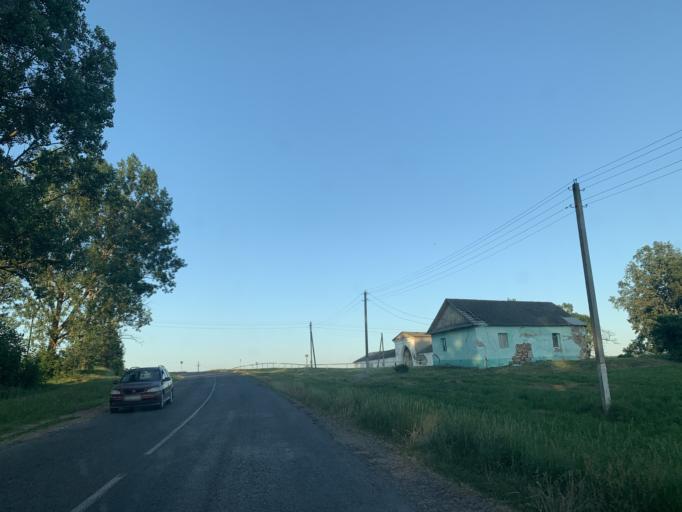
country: BY
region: Minsk
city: Haradzyeya
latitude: 53.2429
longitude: 26.5035
